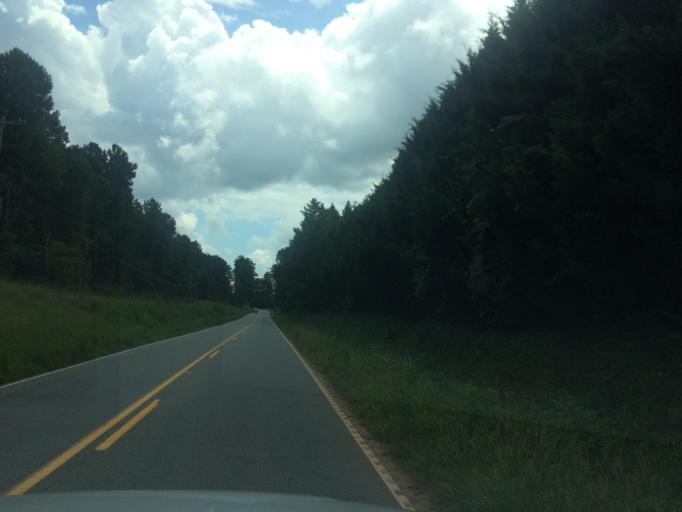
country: US
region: North Carolina
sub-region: Polk County
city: Columbus
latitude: 35.2528
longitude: -82.0962
